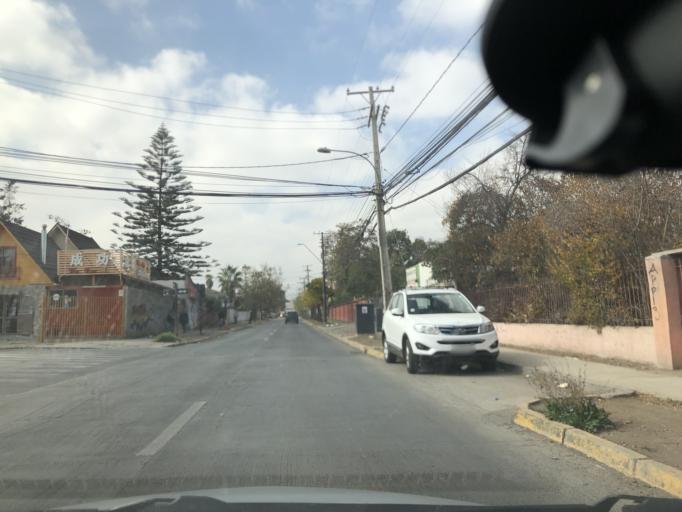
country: CL
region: Santiago Metropolitan
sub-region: Provincia de Cordillera
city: Puente Alto
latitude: -33.6013
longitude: -70.5839
